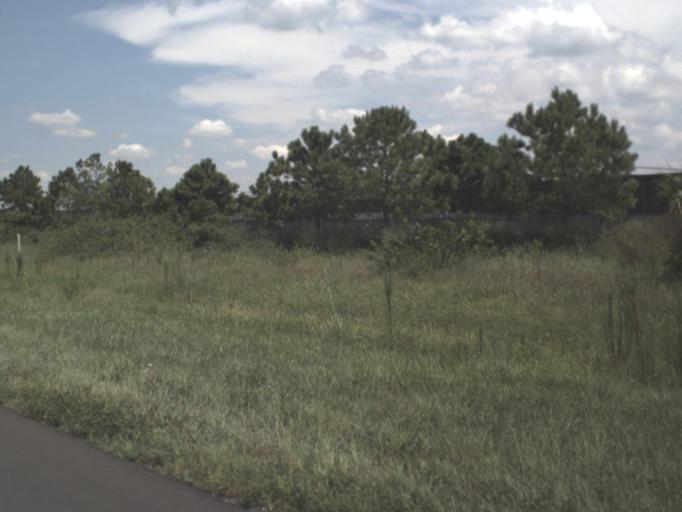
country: US
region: Florida
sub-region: Hillsborough County
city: Ruskin
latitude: 27.6648
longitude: -82.4956
